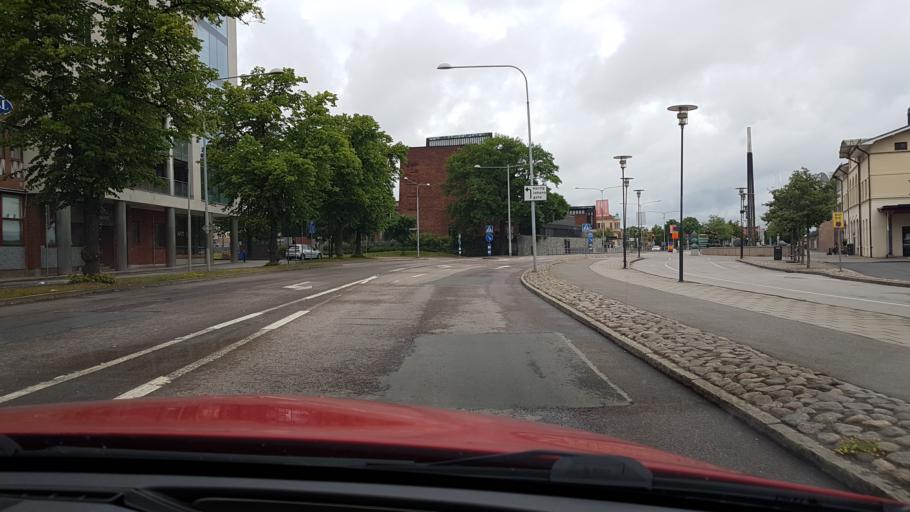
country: SE
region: Vaestra Goetaland
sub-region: Skovde Kommun
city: Skoevde
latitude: 58.3886
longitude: 13.8509
